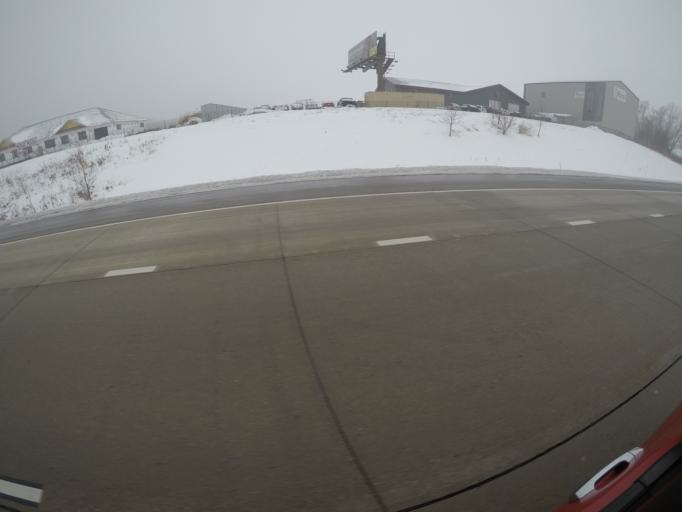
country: US
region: Minnesota
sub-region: Olmsted County
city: Rochester
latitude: 44.0882
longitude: -92.5111
